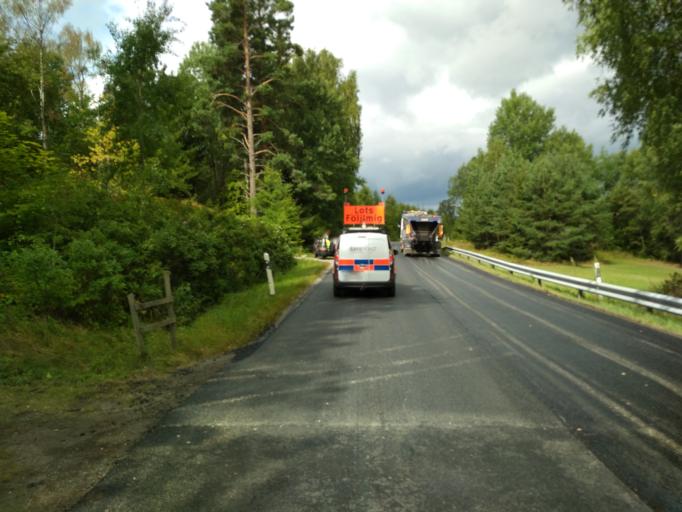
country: SE
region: Soedermanland
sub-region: Flens Kommun
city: Malmkoping
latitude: 59.1576
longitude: 16.6897
